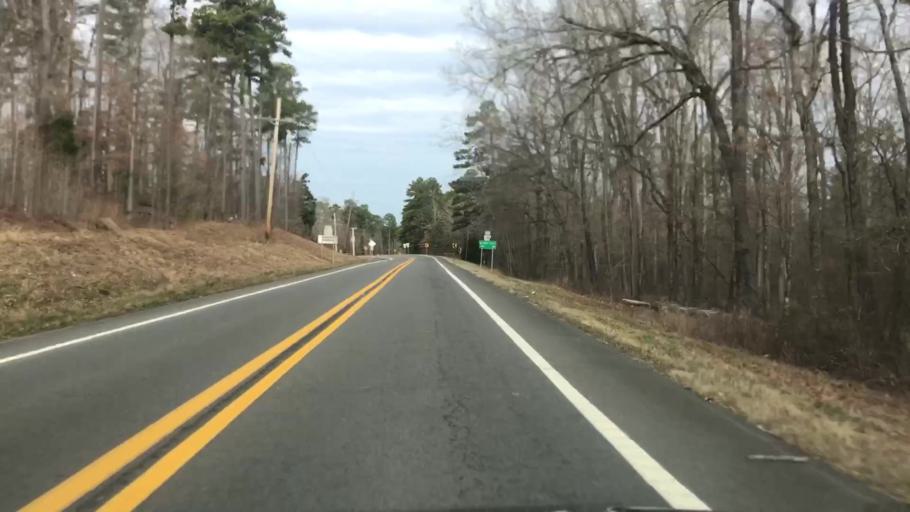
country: US
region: Arkansas
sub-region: Montgomery County
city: Mount Ida
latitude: 34.6070
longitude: -93.6724
